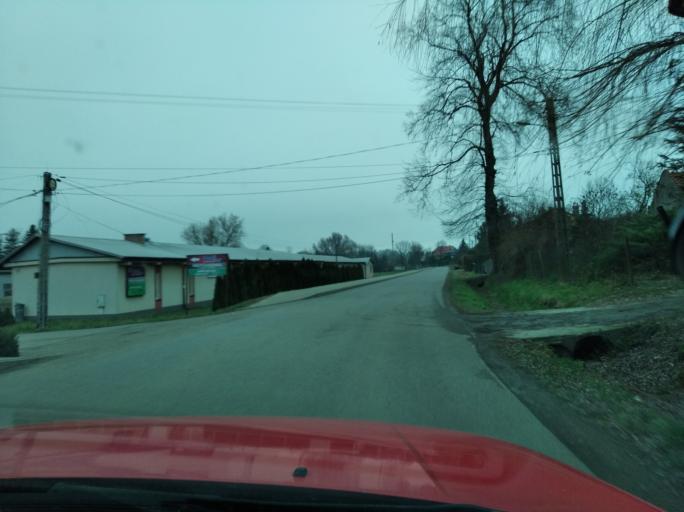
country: PL
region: Subcarpathian Voivodeship
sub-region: Powiat jaroslawski
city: Pawlosiow
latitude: 49.9989
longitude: 22.6483
